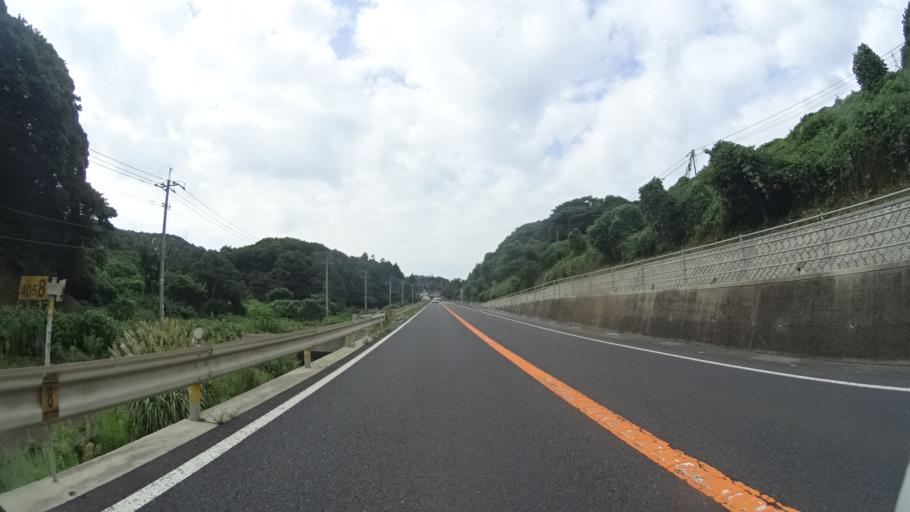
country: JP
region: Shimane
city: Odacho-oda
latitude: 35.1785
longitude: 132.4228
